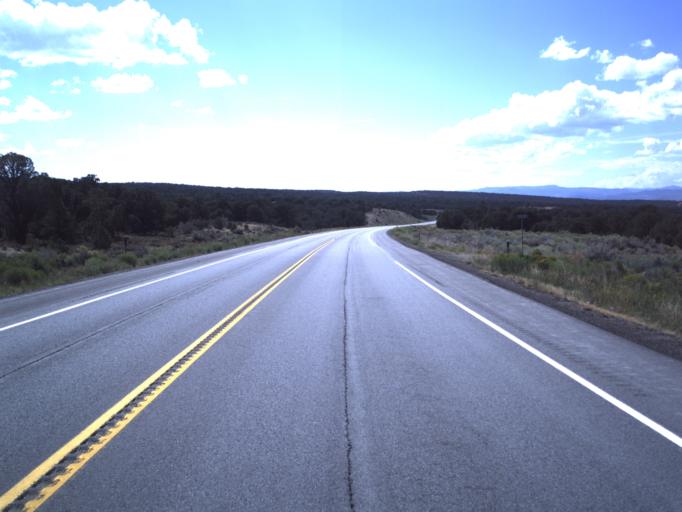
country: US
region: Utah
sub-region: Duchesne County
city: Duchesne
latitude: 40.1819
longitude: -110.6530
